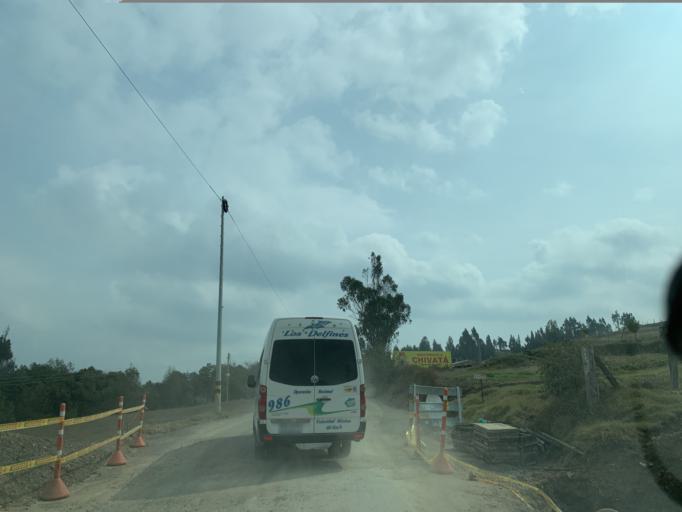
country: CO
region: Boyaca
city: Siachoque
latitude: 5.5411
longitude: -73.3029
